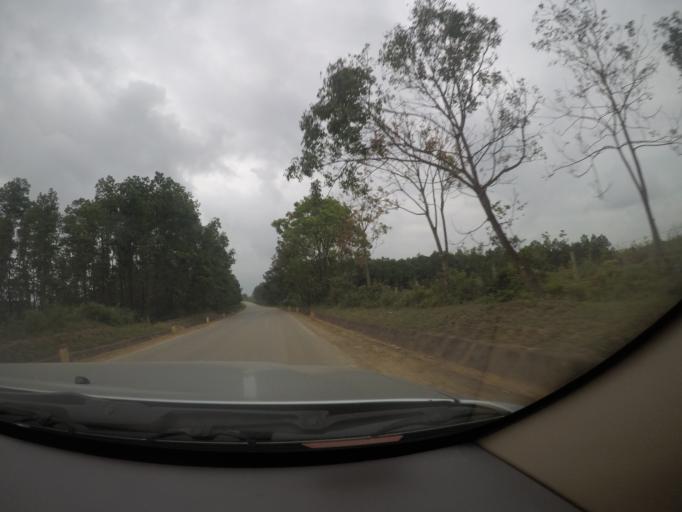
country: VN
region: Quang Tri
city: Cam Lo
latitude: 16.8744
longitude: 106.9927
